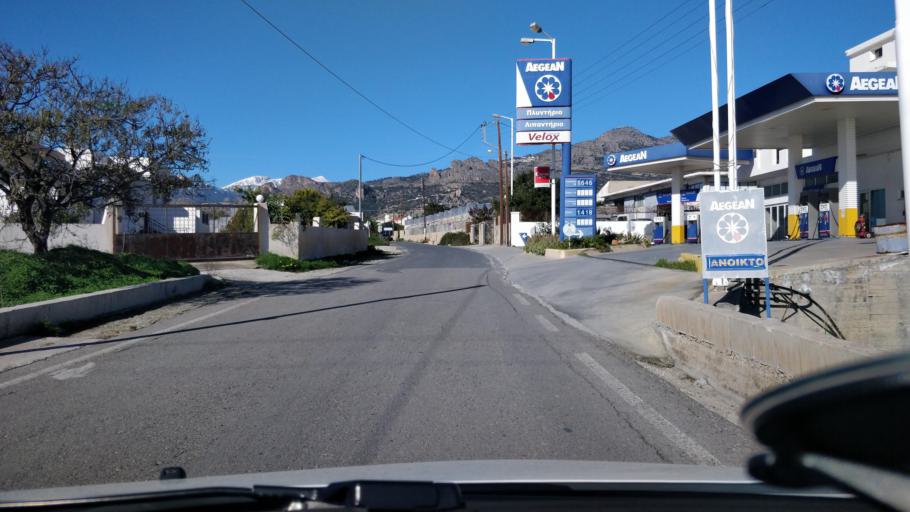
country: GR
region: Crete
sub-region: Nomos Lasithiou
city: Gra Liyia
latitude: 35.0193
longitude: 25.6832
